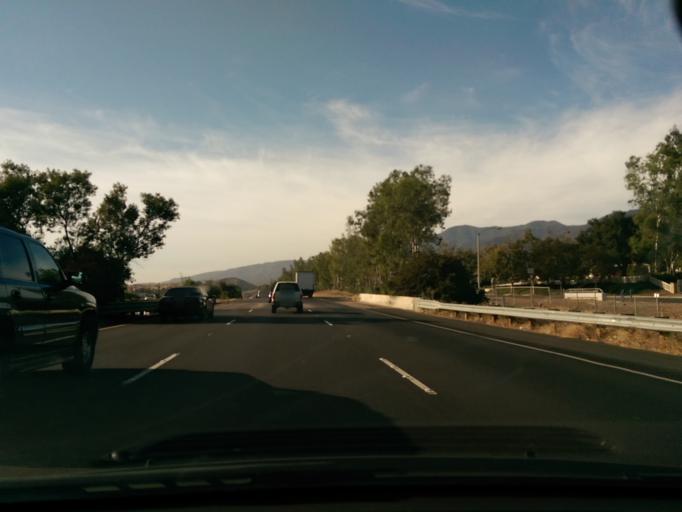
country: US
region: California
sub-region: Riverside County
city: El Cerrito
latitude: 33.7955
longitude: -117.5007
